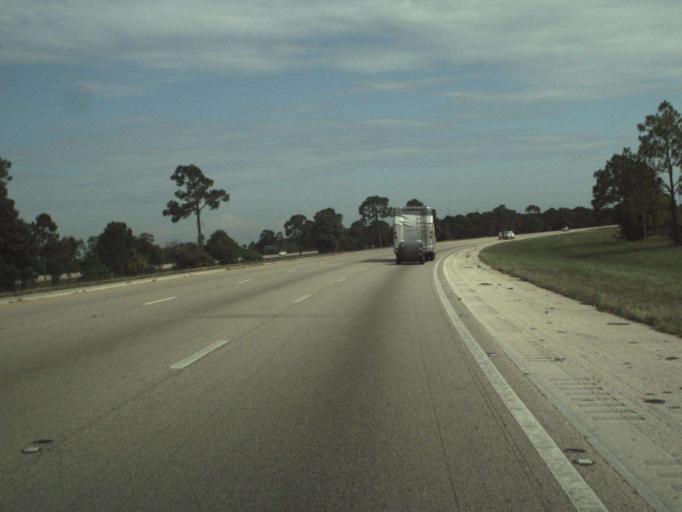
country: US
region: Florida
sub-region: Martin County
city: Palm City
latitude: 27.1512
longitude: -80.3844
